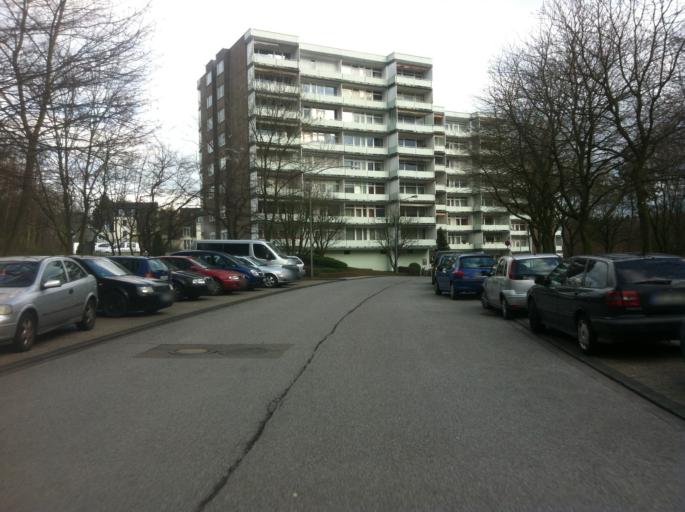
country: DE
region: North Rhine-Westphalia
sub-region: Regierungsbezirk Koln
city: Bergisch Gladbach
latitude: 50.9582
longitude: 7.1684
